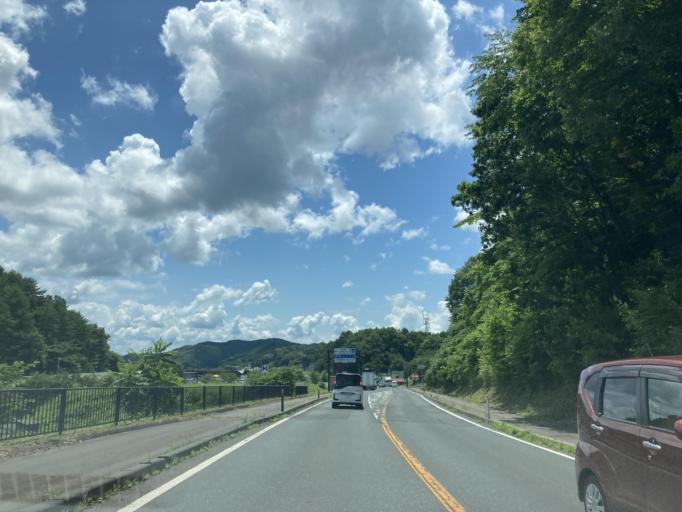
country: JP
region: Iwate
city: Ichinohe
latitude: 39.9709
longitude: 141.2139
